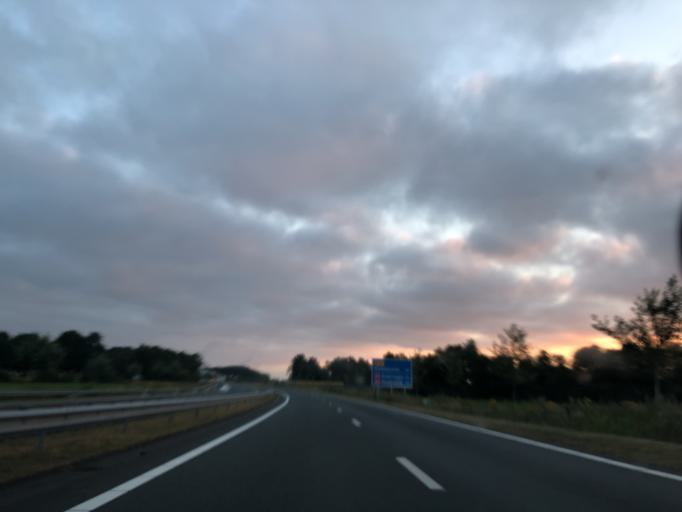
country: NL
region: Groningen
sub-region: Gemeente Veendam
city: Veendam
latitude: 53.1013
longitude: 6.8987
